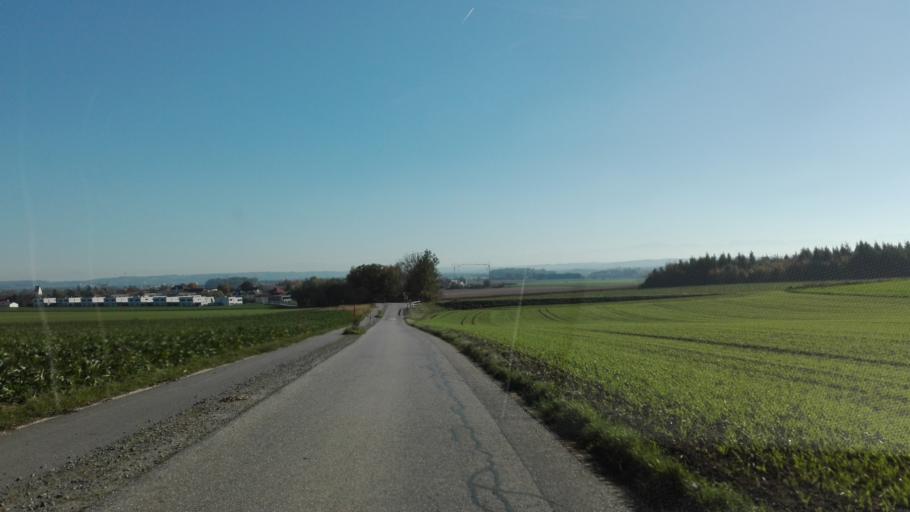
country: AT
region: Upper Austria
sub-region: Politischer Bezirk Linz-Land
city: Pasching
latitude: 48.2637
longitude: 14.1913
